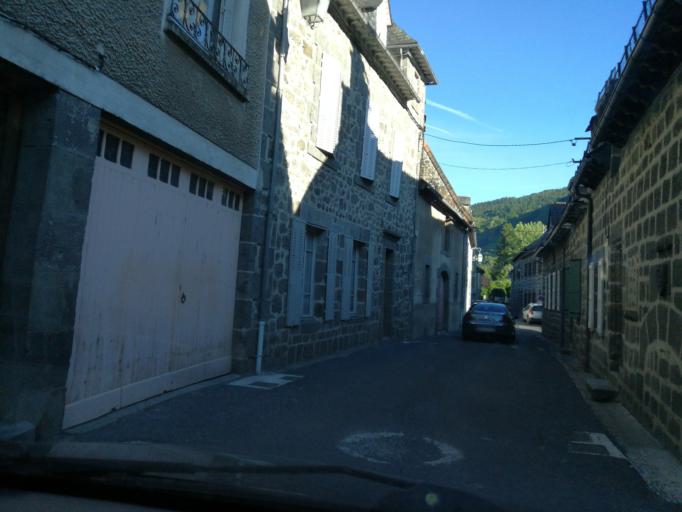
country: FR
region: Auvergne
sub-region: Departement du Cantal
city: Saint-Cernin
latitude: 45.1137
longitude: 2.5036
